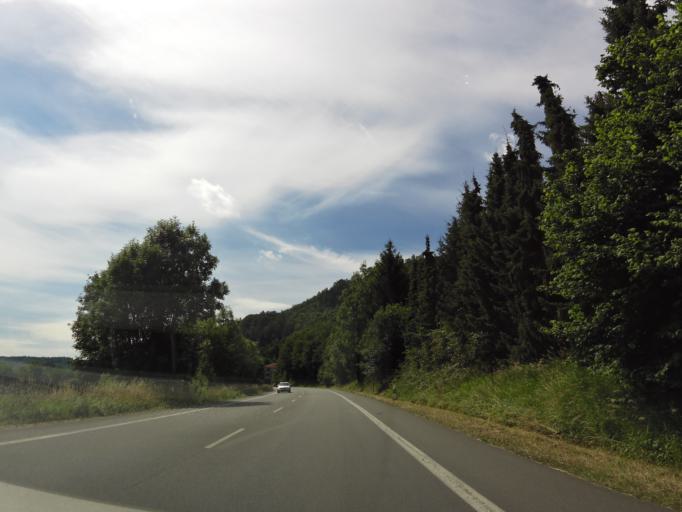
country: DE
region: North Rhine-Westphalia
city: Beverungen
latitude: 51.6526
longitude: 9.3710
